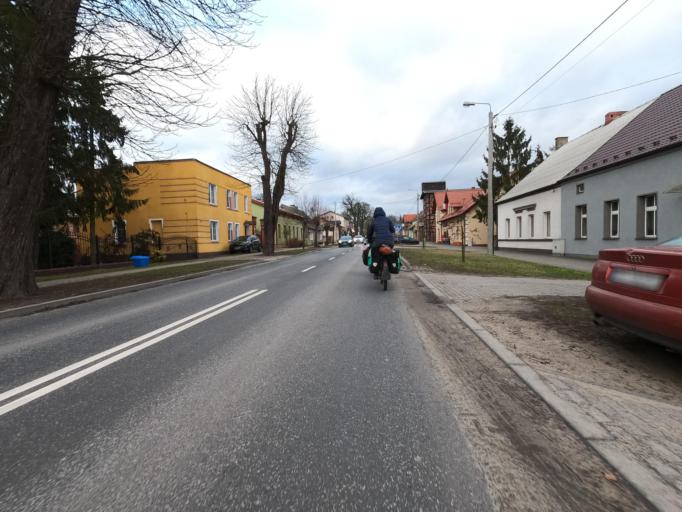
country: PL
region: Greater Poland Voivodeship
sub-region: Powiat pilski
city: Bialosliwie
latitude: 53.0981
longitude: 17.1201
